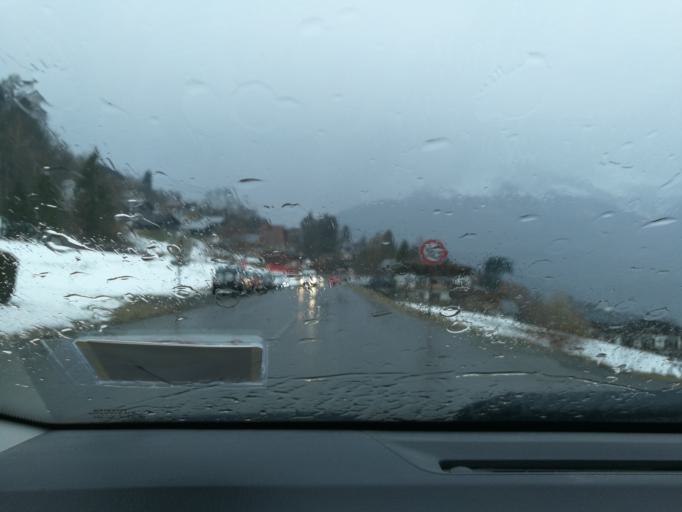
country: FR
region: Rhone-Alpes
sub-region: Departement de la Haute-Savoie
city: Saint-Gervais-les-Bains
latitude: 45.8857
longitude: 6.7035
